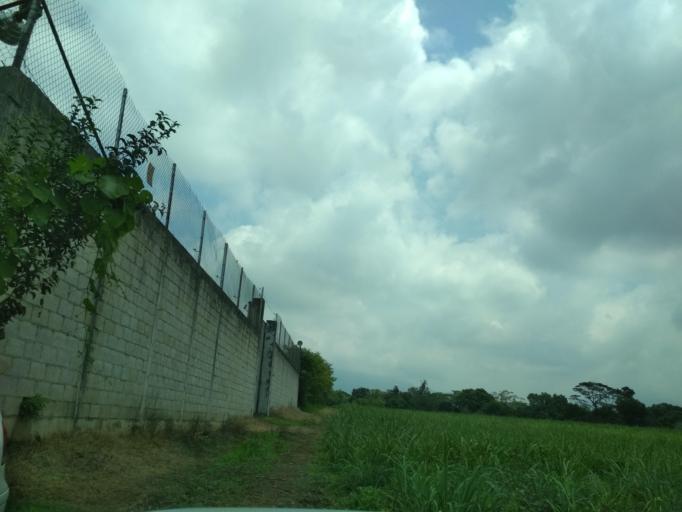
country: MX
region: Veracruz
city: Atzacan
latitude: 18.8794
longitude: -97.0768
